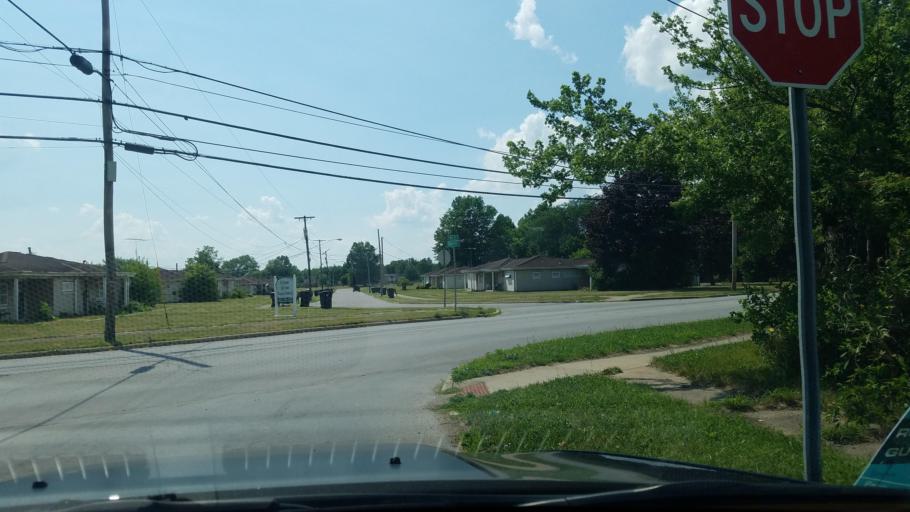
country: US
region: Ohio
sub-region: Trumbull County
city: Bolindale
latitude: 41.2138
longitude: -80.7894
